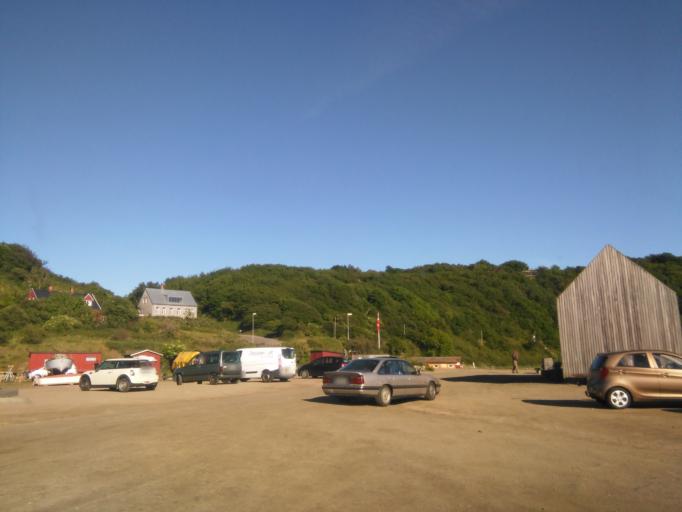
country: DK
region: Capital Region
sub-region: Bornholm Kommune
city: Ronne
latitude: 55.2796
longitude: 14.7552
